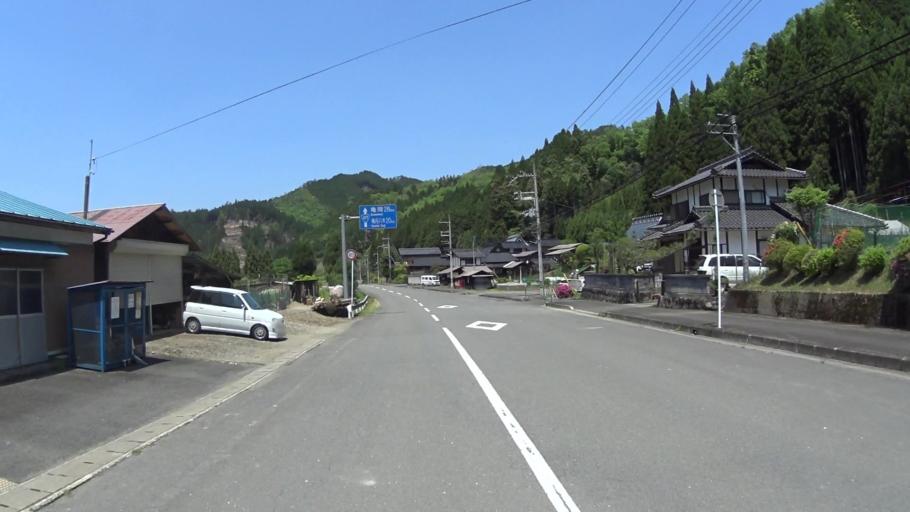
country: JP
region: Kyoto
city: Kameoka
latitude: 35.1345
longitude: 135.6045
